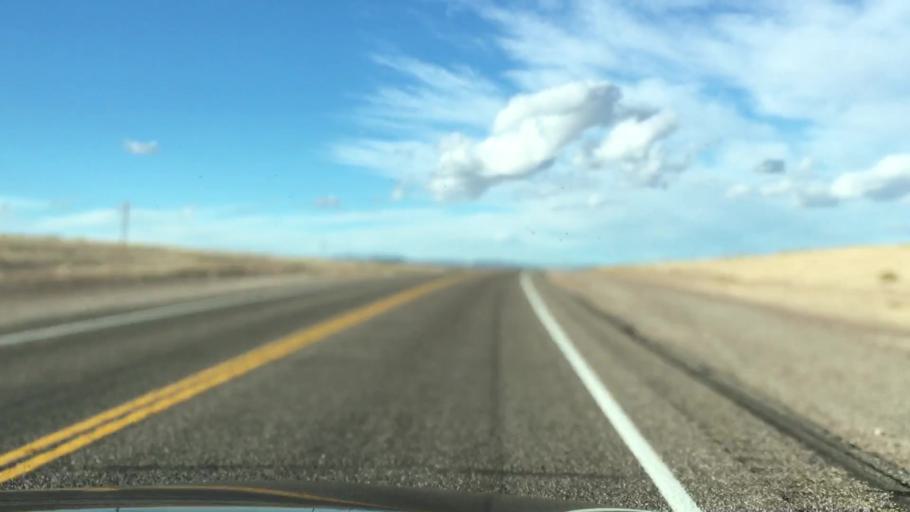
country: US
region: Nevada
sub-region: Esmeralda County
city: Goldfield
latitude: 37.3879
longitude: -117.1438
